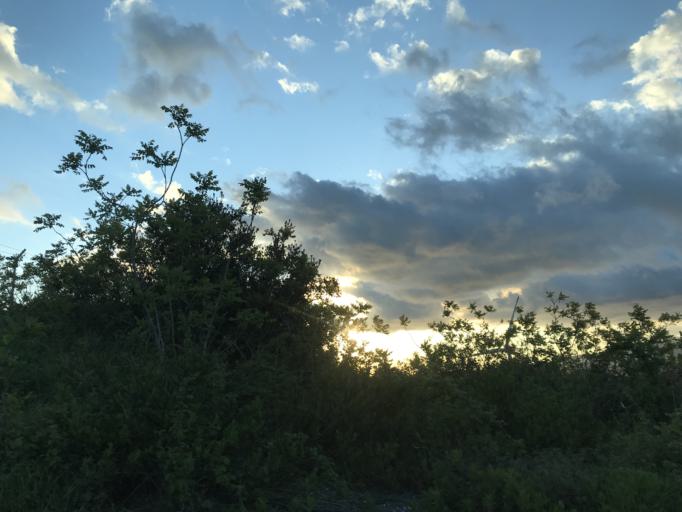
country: TR
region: Hatay
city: Buyukcat
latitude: 36.0925
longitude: 36.0366
